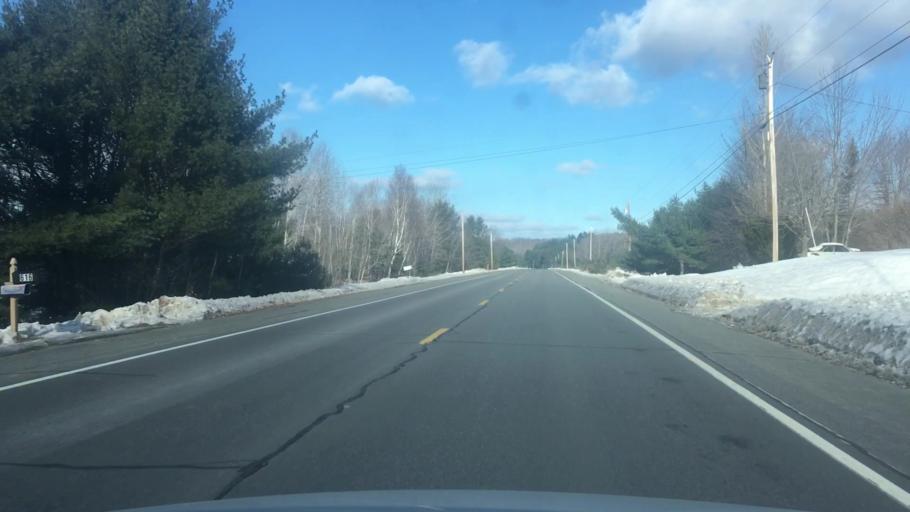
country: US
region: Maine
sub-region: Somerset County
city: Madison
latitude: 45.0201
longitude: -69.8576
